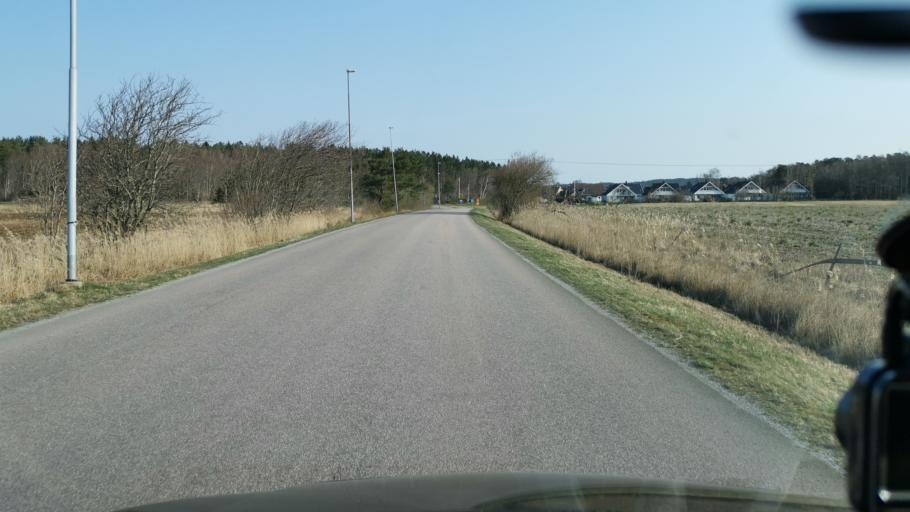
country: SE
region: Vaestra Goetaland
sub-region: Kungalvs Kommun
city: Kode
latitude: 57.9410
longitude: 11.8354
